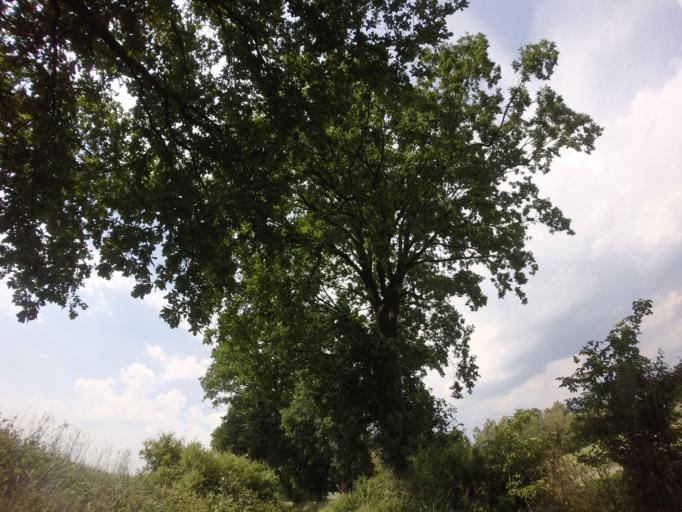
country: PL
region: West Pomeranian Voivodeship
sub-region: Powiat choszczenski
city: Krzecin
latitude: 53.1285
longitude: 15.5902
